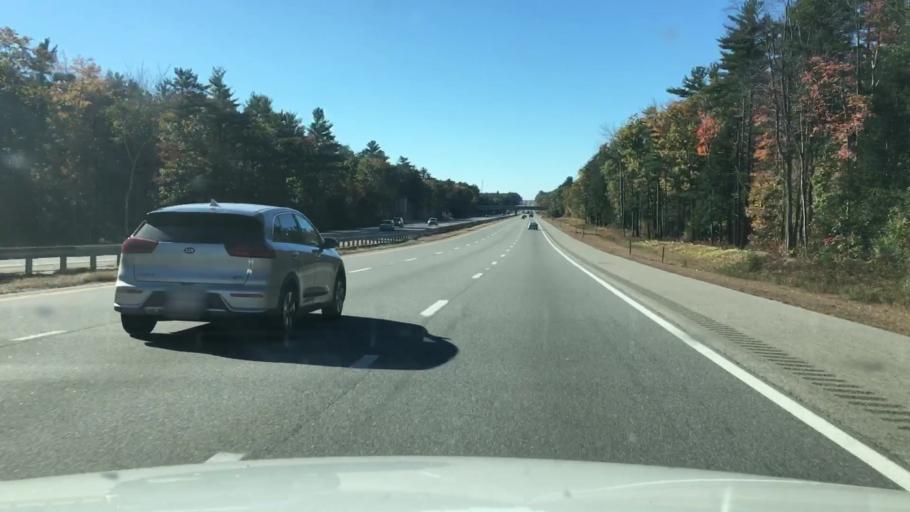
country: US
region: Maine
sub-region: York County
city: West Kennebunk
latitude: 43.3878
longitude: -70.5724
